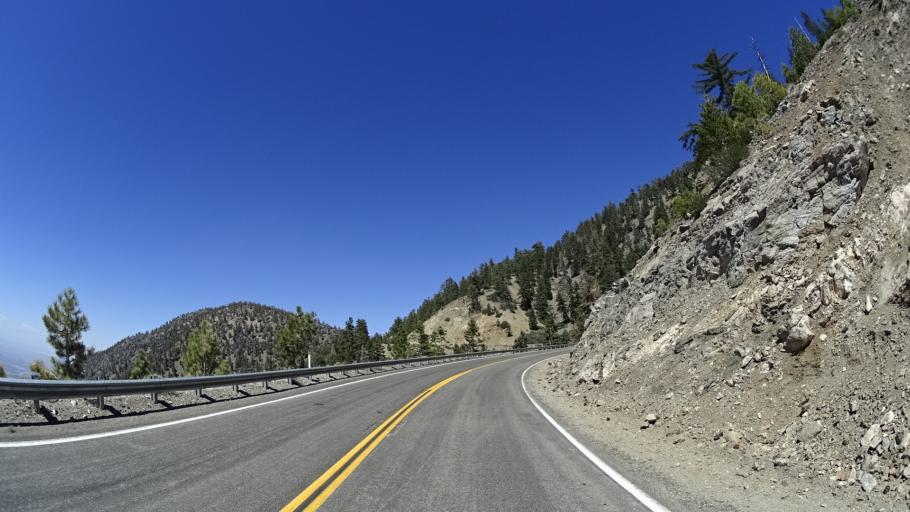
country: US
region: California
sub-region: San Bernardino County
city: Wrightwood
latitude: 34.3599
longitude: -117.8125
